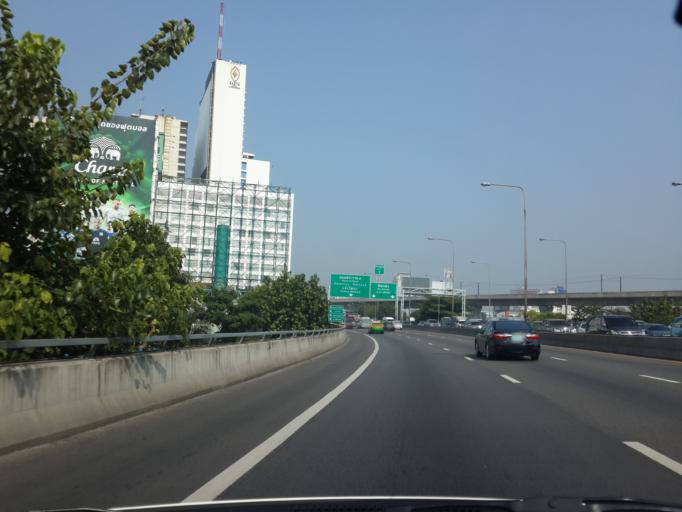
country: TH
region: Bangkok
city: Ratchathewi
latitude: 13.7520
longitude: 100.5487
